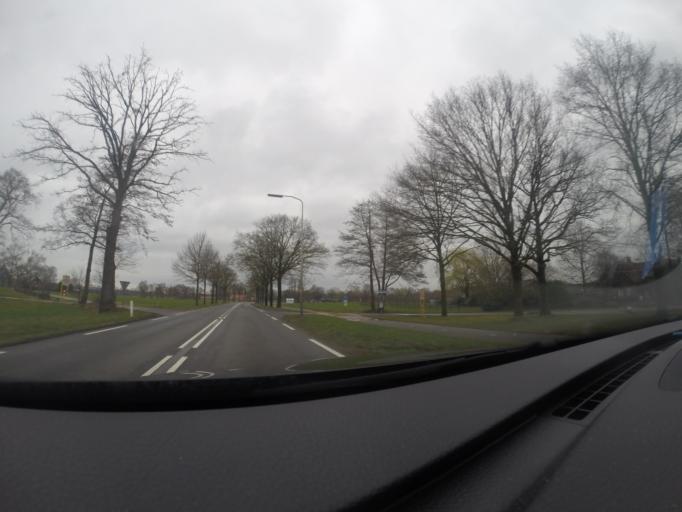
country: NL
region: Overijssel
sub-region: Gemeente Hof van Twente
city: Delden
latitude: 52.2377
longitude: 6.6913
